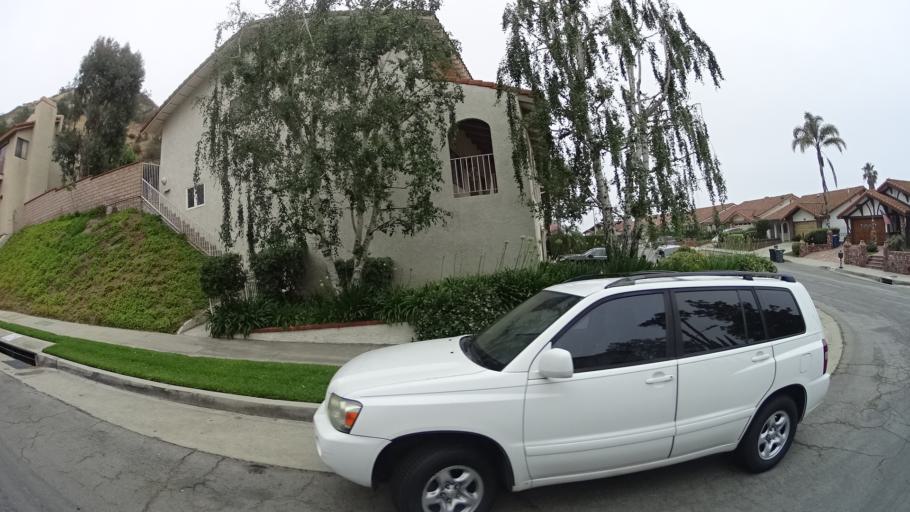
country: US
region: California
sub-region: Los Angeles County
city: Burbank
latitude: 34.1950
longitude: -118.2903
